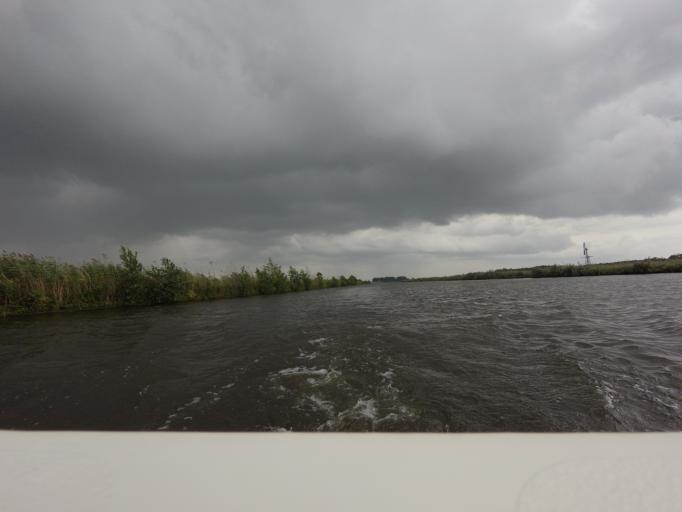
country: NL
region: Friesland
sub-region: Gemeente Smallingerland
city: Oudega
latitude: 53.1171
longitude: 5.9463
